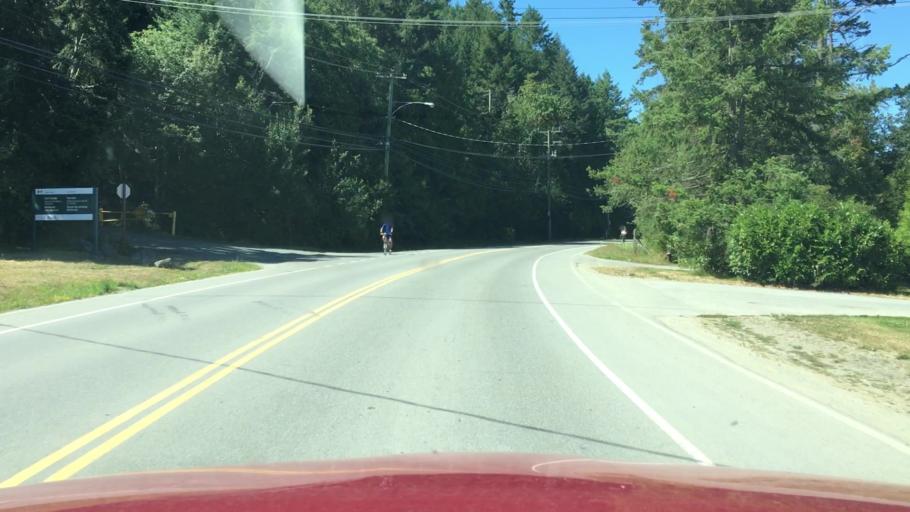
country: CA
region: British Columbia
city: North Saanich
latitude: 48.6728
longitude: -123.4238
